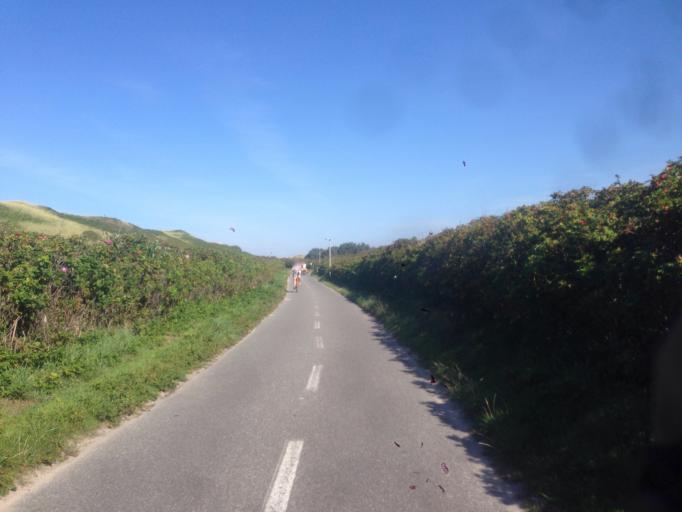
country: DE
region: Schleswig-Holstein
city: Westerland
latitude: 54.9182
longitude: 8.3057
